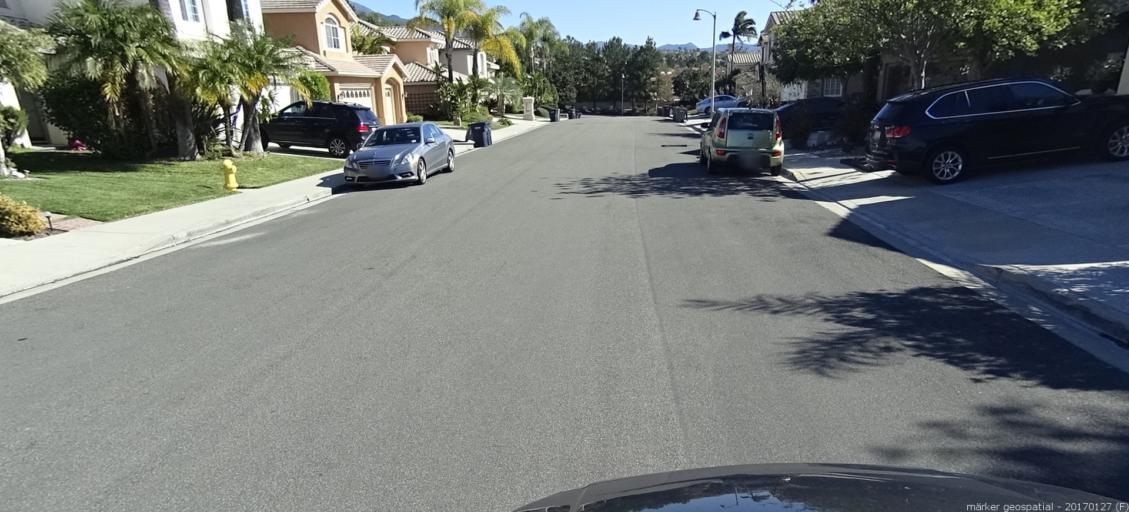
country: US
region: California
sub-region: Orange County
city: Foothill Ranch
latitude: 33.6882
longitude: -117.6631
